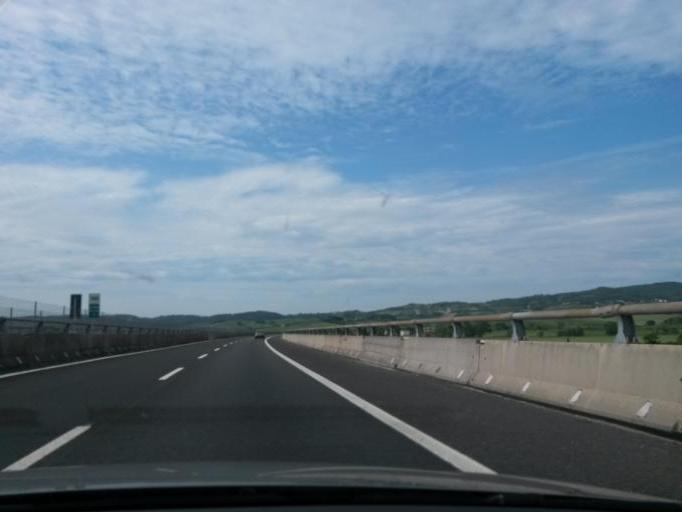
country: IT
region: Tuscany
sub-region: Provincia di Livorno
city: Rosignano Marittimo
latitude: 43.4443
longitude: 10.4932
